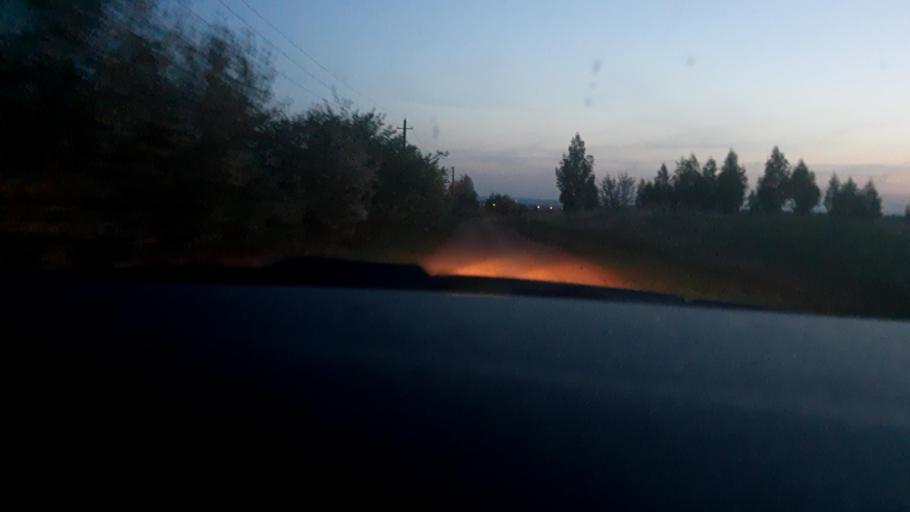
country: RU
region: Bashkortostan
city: Iglino
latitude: 54.7601
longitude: 56.3328
